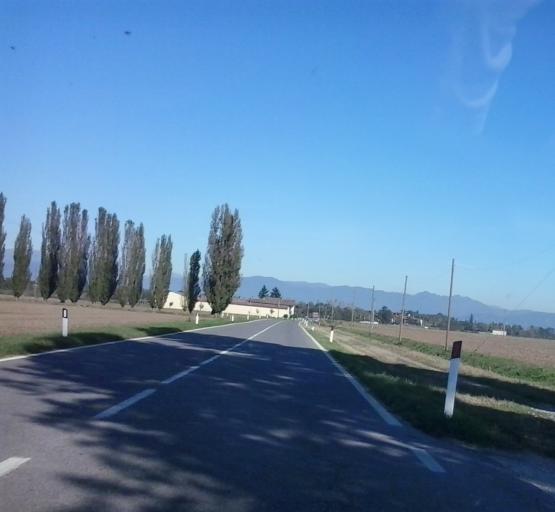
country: IT
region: Lombardy
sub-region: Provincia di Brescia
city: Poncarale
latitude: 45.4400
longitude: 10.1601
